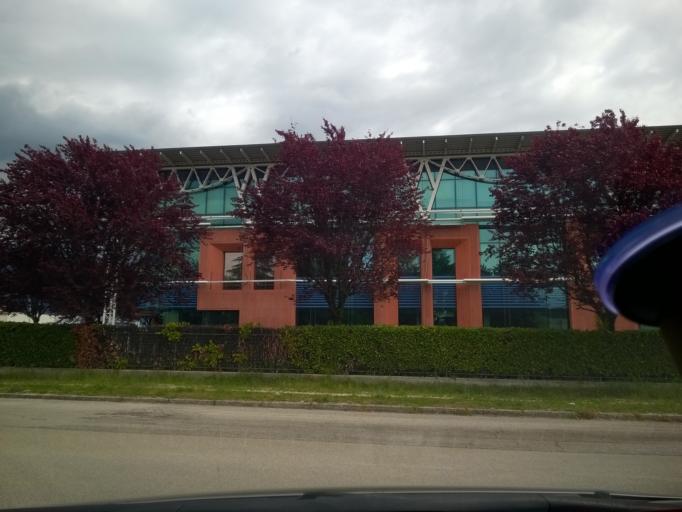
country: IT
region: Veneto
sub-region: Provincia di Treviso
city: Scomigo
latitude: 45.9473
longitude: 12.3160
